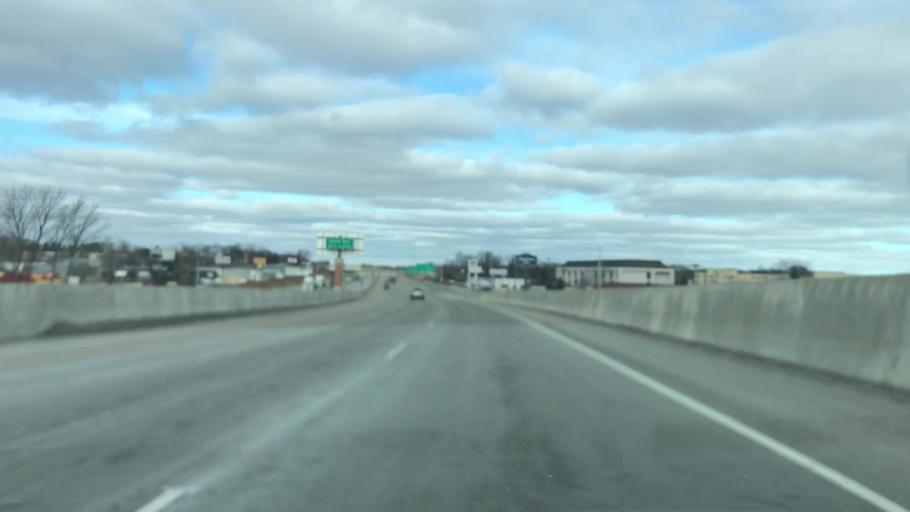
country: US
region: Wisconsin
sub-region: Brown County
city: Ashwaubenon
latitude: 44.4700
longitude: -88.0791
